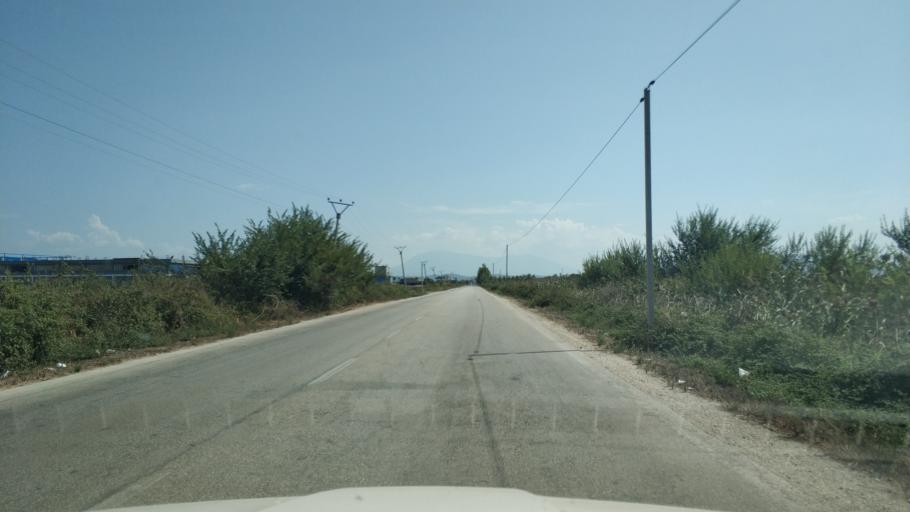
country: AL
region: Fier
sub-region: Rrethi i Lushnjes
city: Krutja e Poshtme
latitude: 40.8837
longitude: 19.6572
